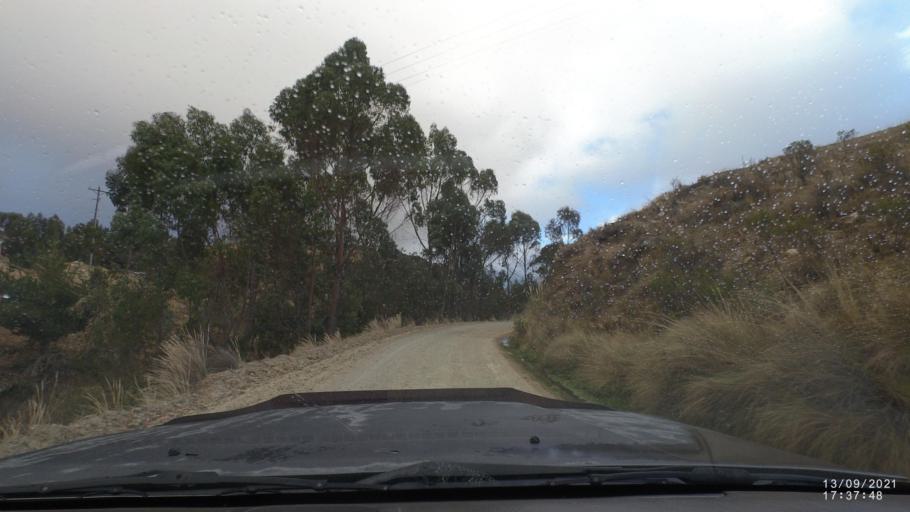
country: BO
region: Cochabamba
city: Colomi
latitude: -17.3620
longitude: -65.8046
